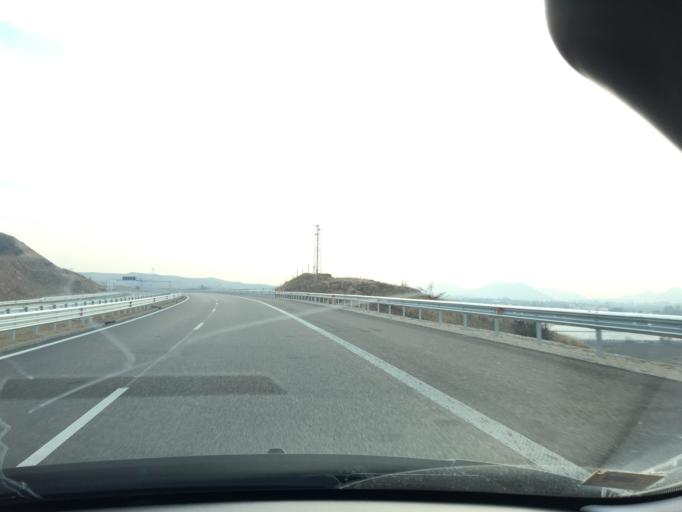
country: BG
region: Blagoevgrad
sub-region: Obshtina Sandanski
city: Sandanski
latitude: 41.5308
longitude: 23.2602
